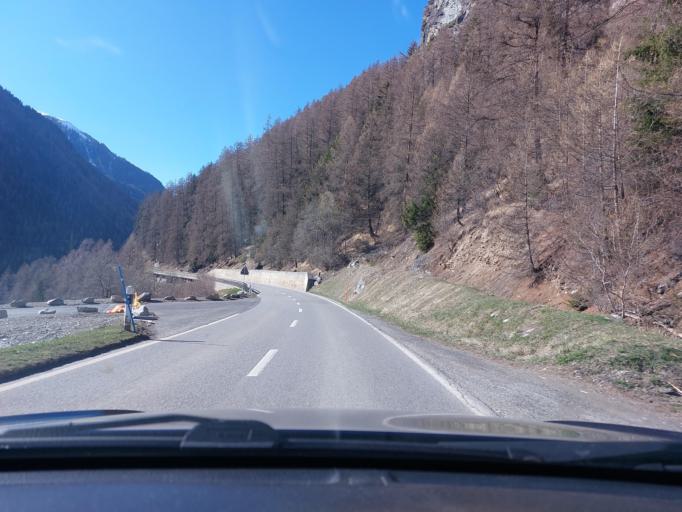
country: CH
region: Valais
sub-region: Herens District
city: Evolene
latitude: 46.1246
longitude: 7.4837
